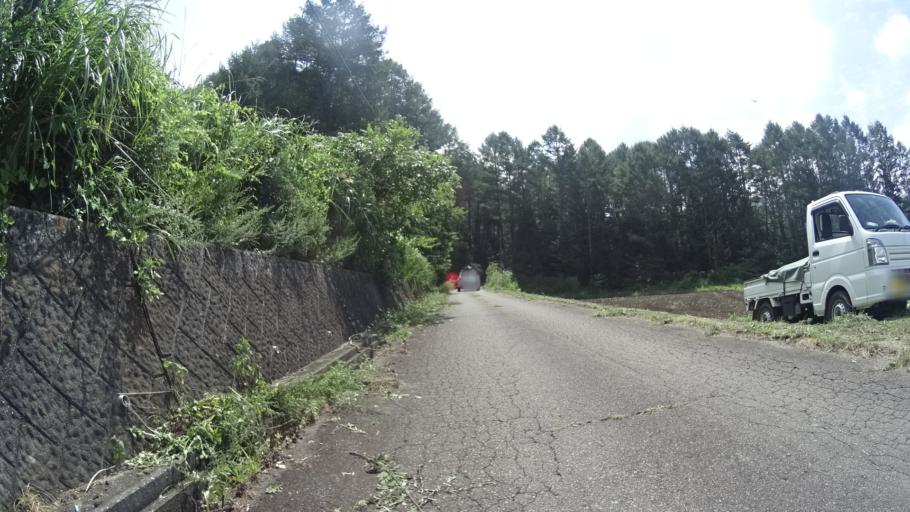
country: JP
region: Yamanashi
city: Nirasaki
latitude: 35.8890
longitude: 138.4751
